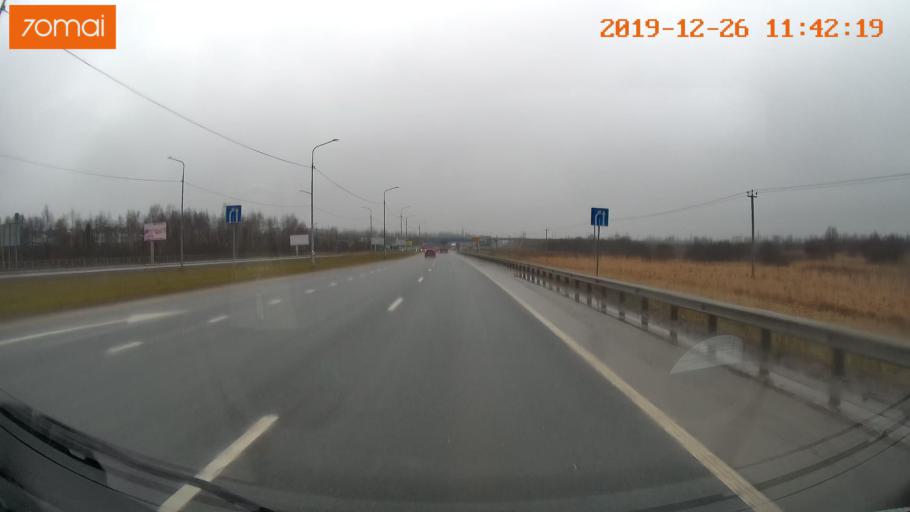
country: RU
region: Vologda
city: Sheksna
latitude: 59.2116
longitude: 38.5239
